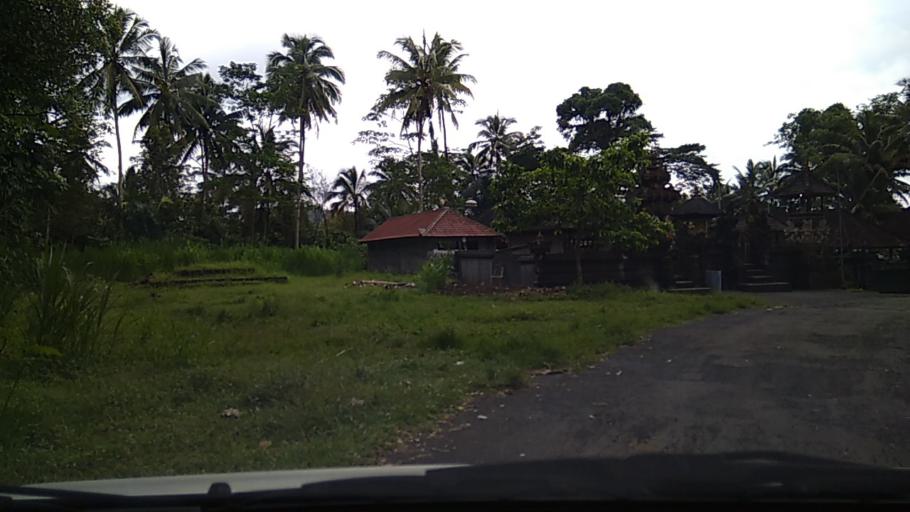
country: ID
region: Bali
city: Banjar Kubu
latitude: -8.4402
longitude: 115.3874
